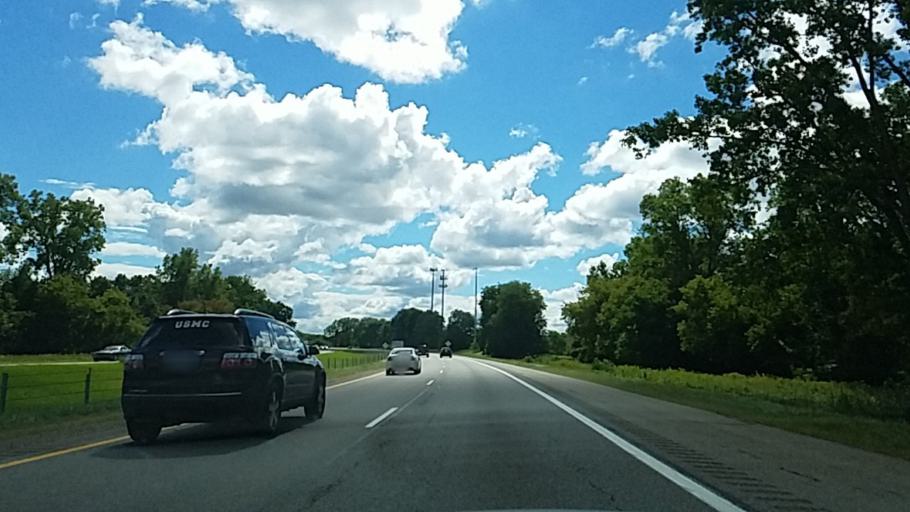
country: US
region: Michigan
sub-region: Livingston County
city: Brighton
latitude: 42.5529
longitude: -83.7477
